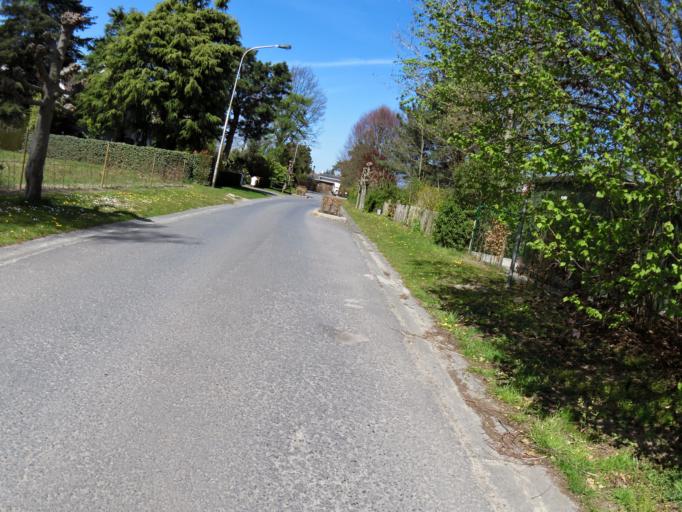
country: BE
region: Flanders
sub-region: Provincie Oost-Vlaanderen
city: Sint-Martens-Latem
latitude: 51.0186
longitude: 3.6503
